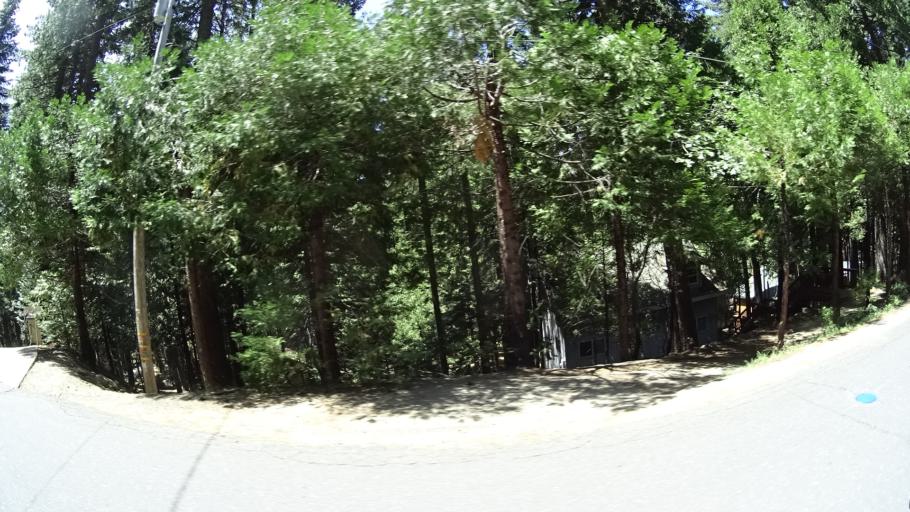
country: US
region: California
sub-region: Calaveras County
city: Arnold
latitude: 38.3006
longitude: -120.2604
